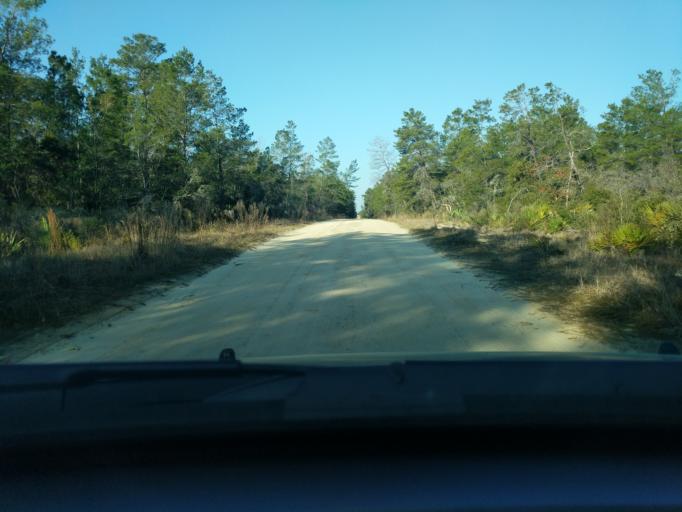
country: US
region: Florida
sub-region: Marion County
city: Silver Springs Shores
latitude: 29.2263
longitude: -81.7921
